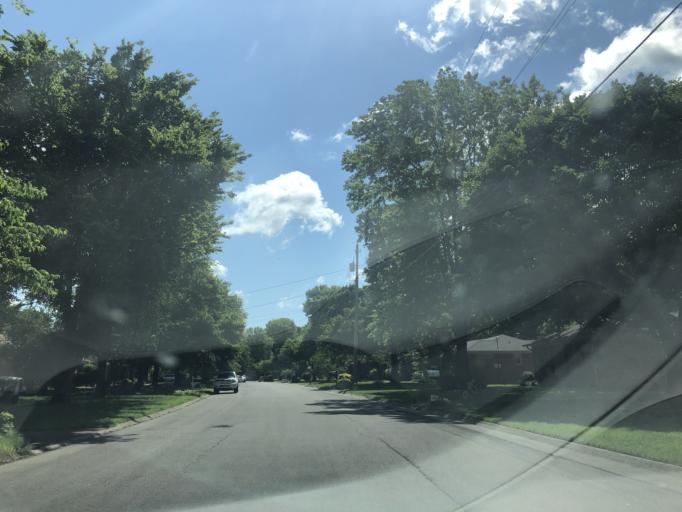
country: US
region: Tennessee
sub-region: Davidson County
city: Belle Meade
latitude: 36.0681
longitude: -86.9371
